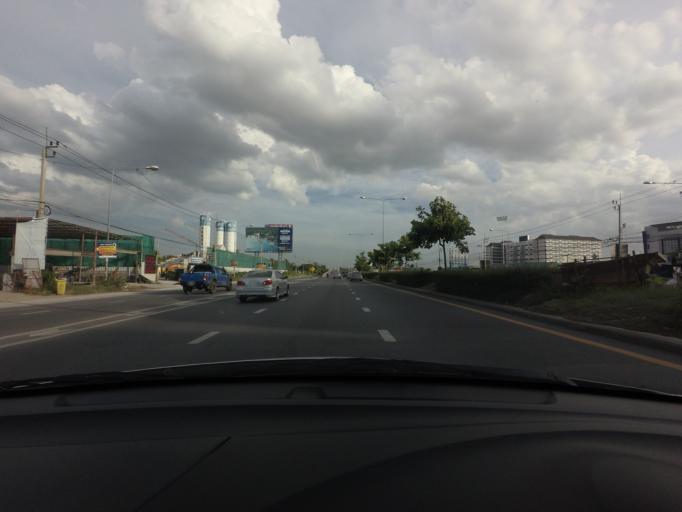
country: TH
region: Nonthaburi
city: Bang Bua Thong
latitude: 13.9014
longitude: 100.4499
